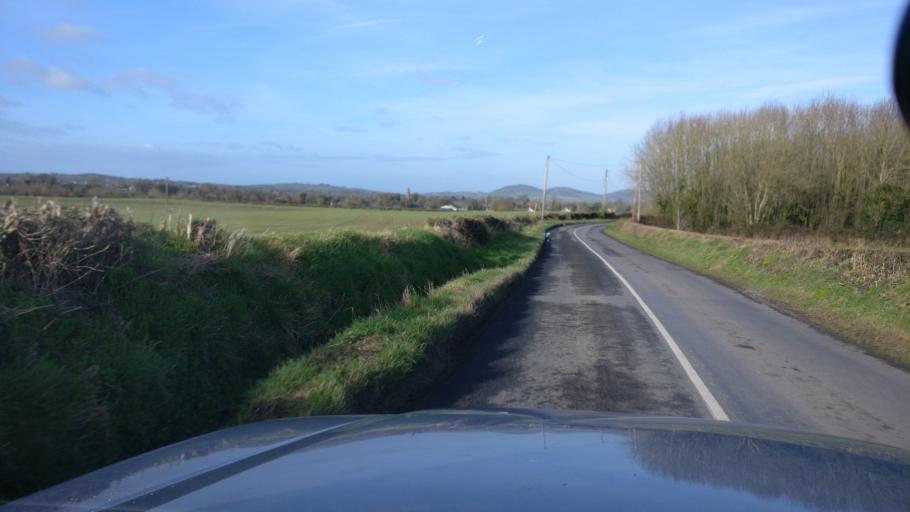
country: IE
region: Leinster
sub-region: Laois
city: Stradbally
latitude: 52.9527
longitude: -7.1987
